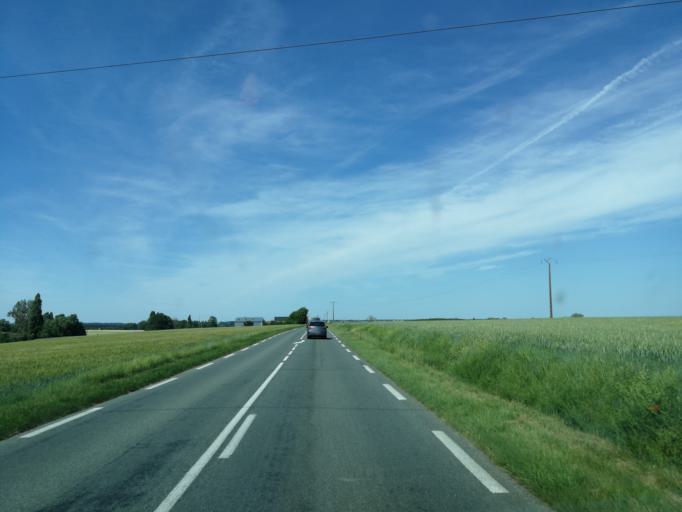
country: FR
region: Poitou-Charentes
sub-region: Departement de la Vienne
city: Loudun
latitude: 47.0679
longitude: 0.1671
